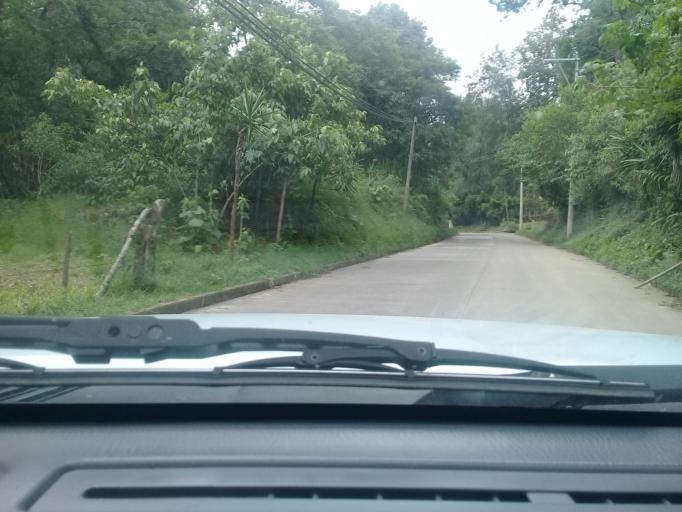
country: MX
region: Veracruz
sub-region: Tlalnelhuayocan
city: Guadalupe Victoria
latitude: 19.5450
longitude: -96.9690
